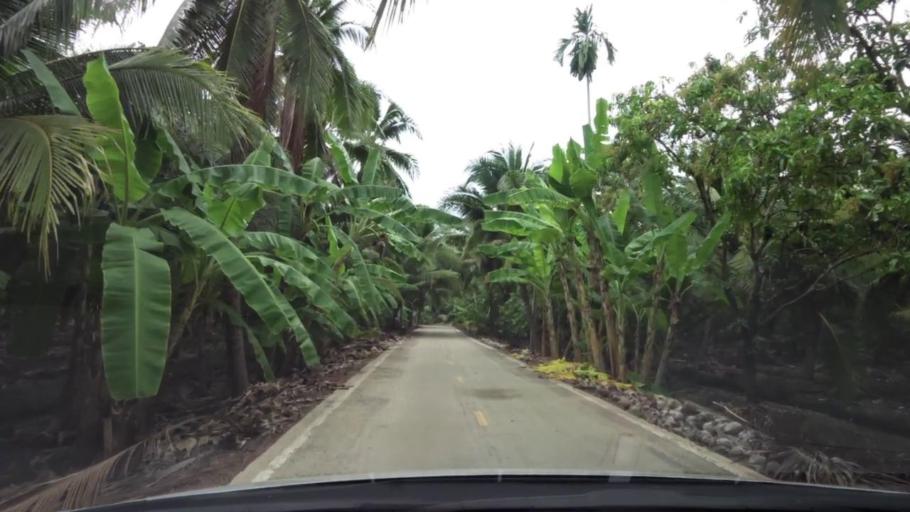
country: TH
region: Ratchaburi
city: Damnoen Saduak
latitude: 13.5496
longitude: 99.9898
